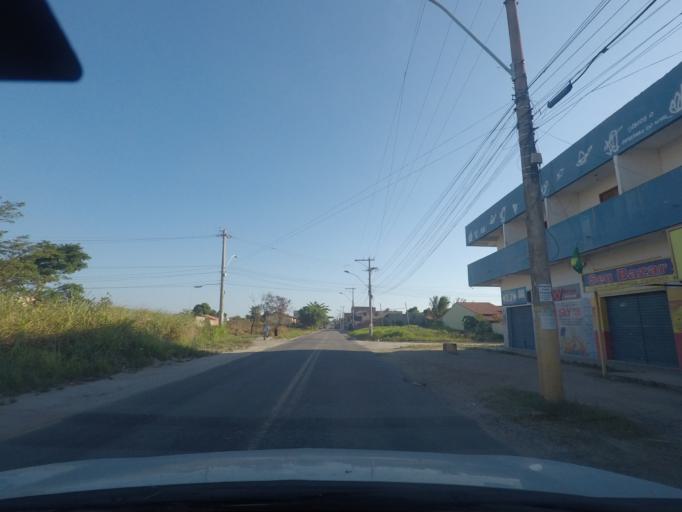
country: BR
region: Rio de Janeiro
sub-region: Marica
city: Marica
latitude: -22.9617
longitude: -42.9424
